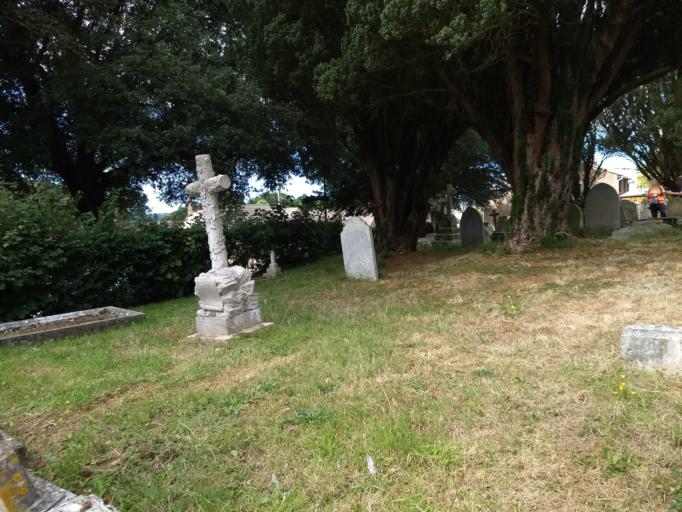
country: GB
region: England
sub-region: Isle of Wight
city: Newchurch
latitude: 50.7096
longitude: -1.2060
